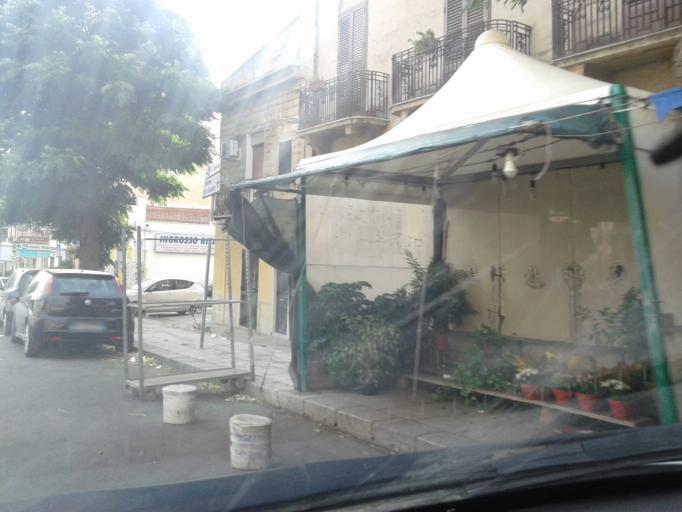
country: IT
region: Sicily
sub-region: Palermo
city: Monreale
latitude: 38.0943
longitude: 13.3087
